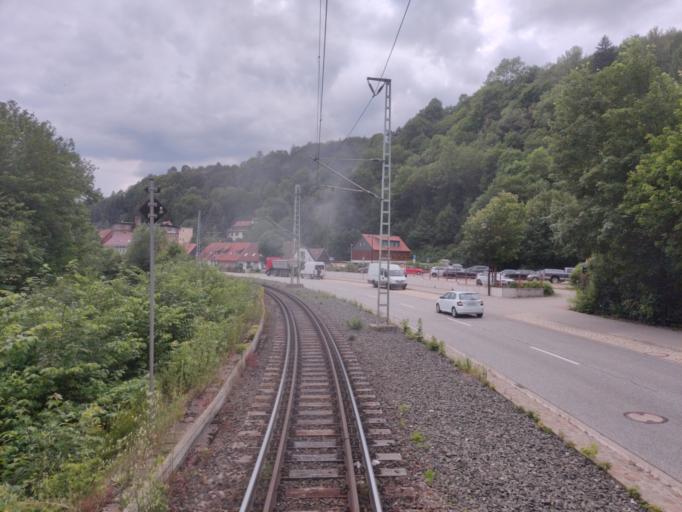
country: DE
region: Saxony-Anhalt
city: Rubeland
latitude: 51.7580
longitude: 10.8498
